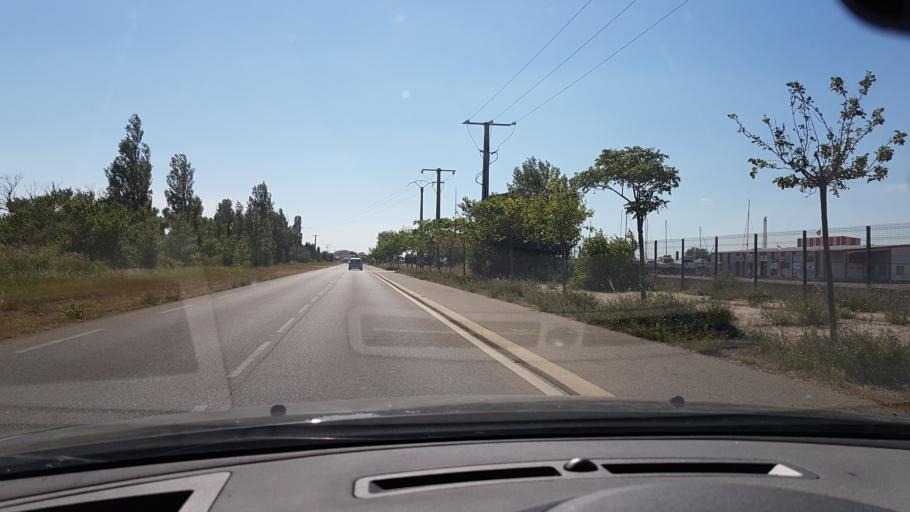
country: FR
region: Provence-Alpes-Cote d'Azur
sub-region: Departement des Bouches-du-Rhone
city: Port-Saint-Louis-du-Rhone
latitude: 43.3844
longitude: 4.8219
